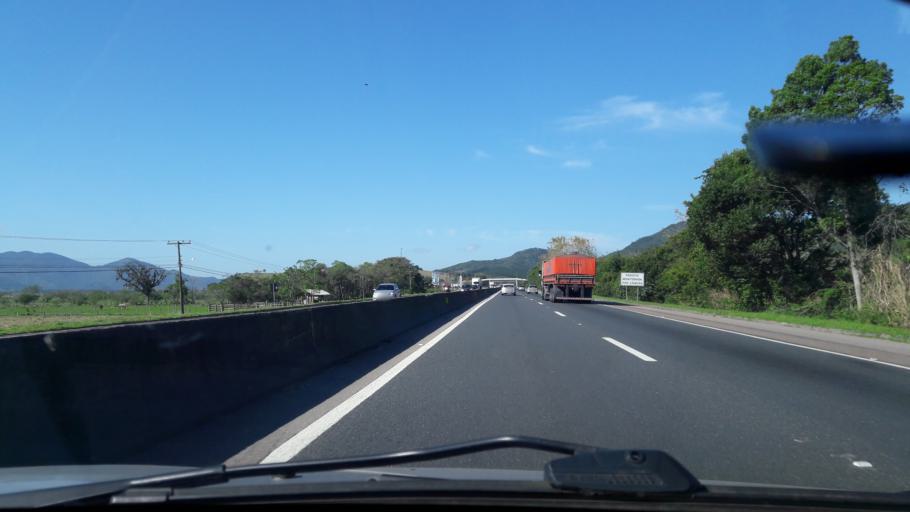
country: BR
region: Santa Catarina
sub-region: Tijucas
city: Tijucas
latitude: -27.2956
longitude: -48.6313
